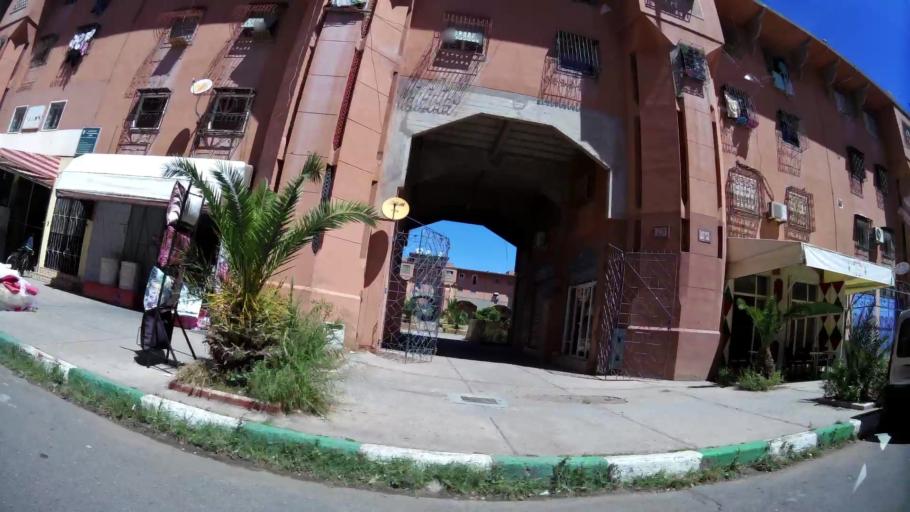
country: MA
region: Marrakech-Tensift-Al Haouz
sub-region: Marrakech
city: Marrakesh
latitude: 31.6338
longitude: -8.0664
